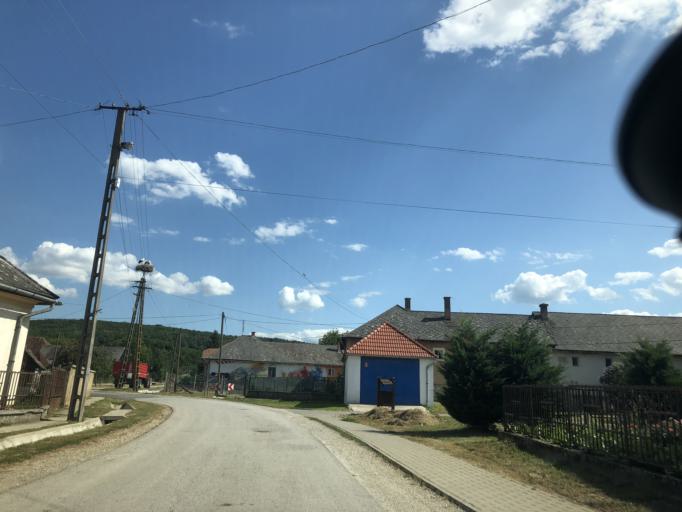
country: HU
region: Borsod-Abauj-Zemplen
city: Szendro
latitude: 48.5419
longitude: 20.8038
